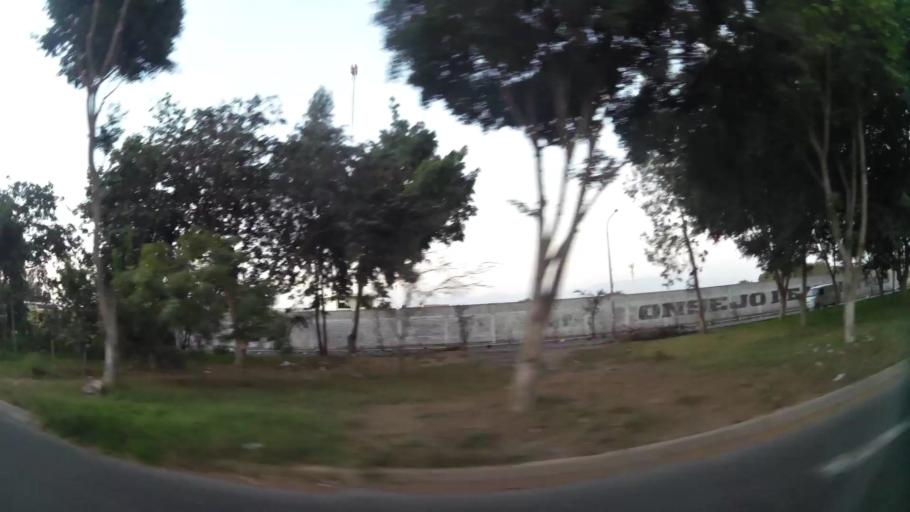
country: PE
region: Ica
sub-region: Provincia de Ica
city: Ica
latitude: -14.0804
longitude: -75.7312
